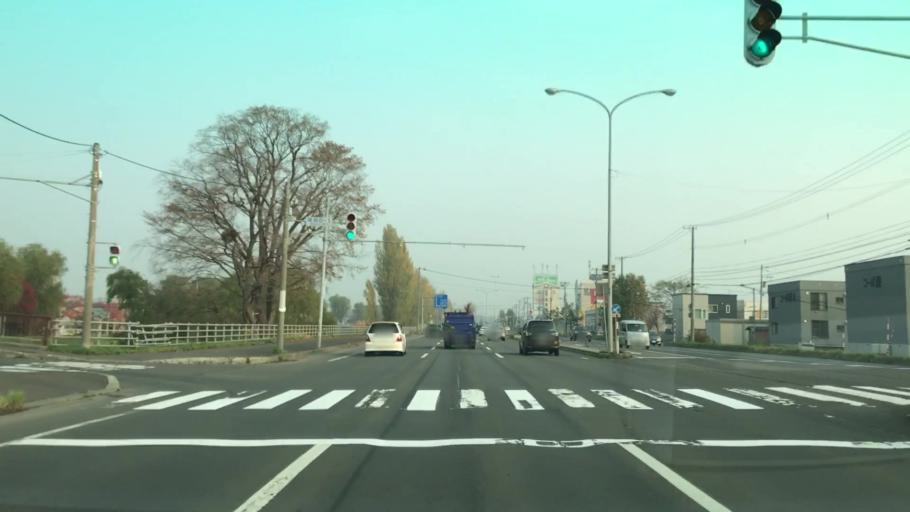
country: JP
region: Hokkaido
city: Ishikari
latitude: 43.1547
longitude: 141.3519
